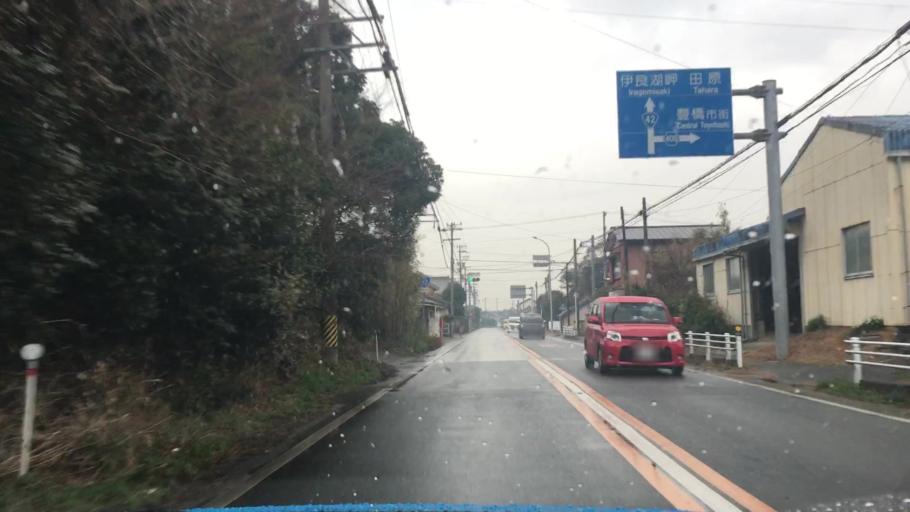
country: JP
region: Aichi
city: Tahara
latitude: 34.6620
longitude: 137.3684
